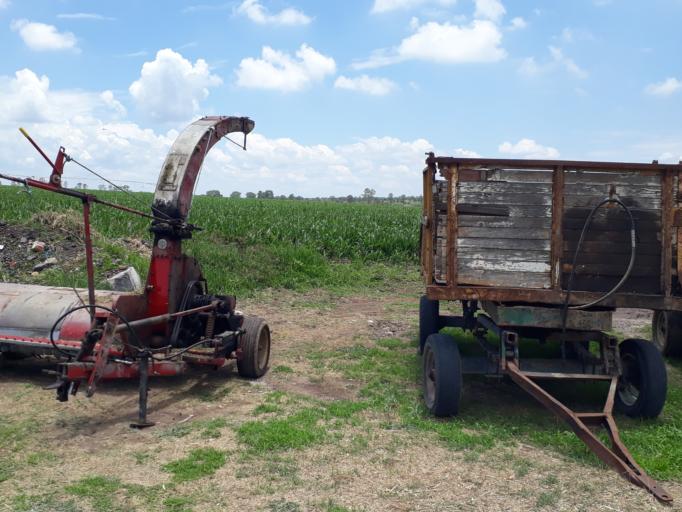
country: MX
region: Aguascalientes
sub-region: Aguascalientes
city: La Loma de los Negritos
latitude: 21.8257
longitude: -102.3282
